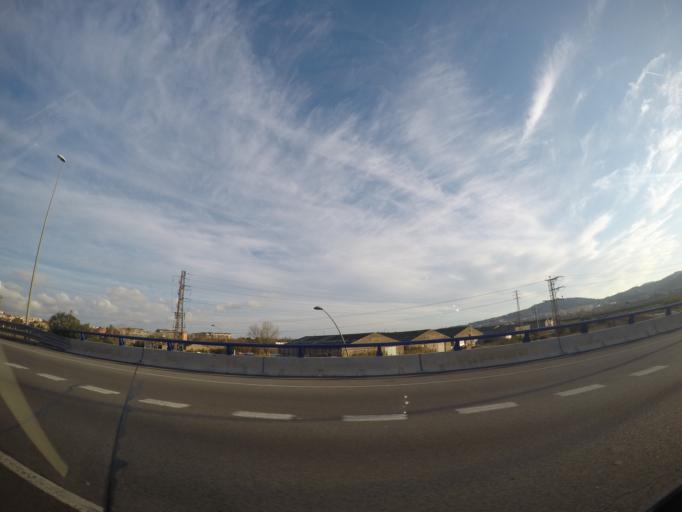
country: ES
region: Catalonia
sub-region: Provincia de Barcelona
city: Sant Feliu de Llobregat
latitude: 41.3729
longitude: 2.0429
